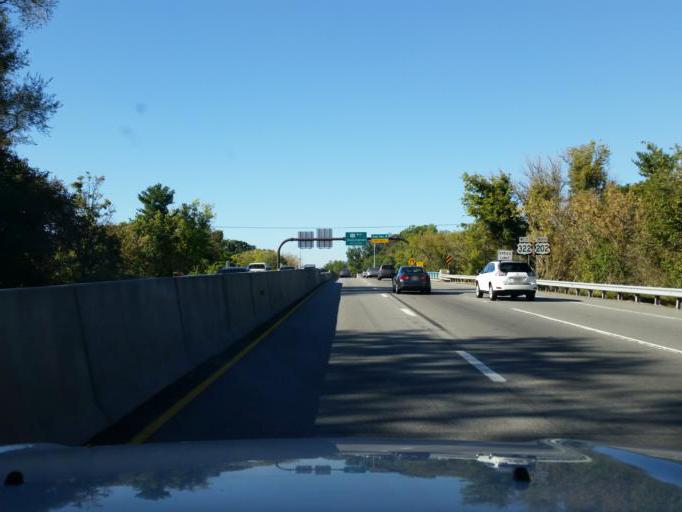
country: US
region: Pennsylvania
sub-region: Chester County
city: West Chester
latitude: 39.9703
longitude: -75.5827
